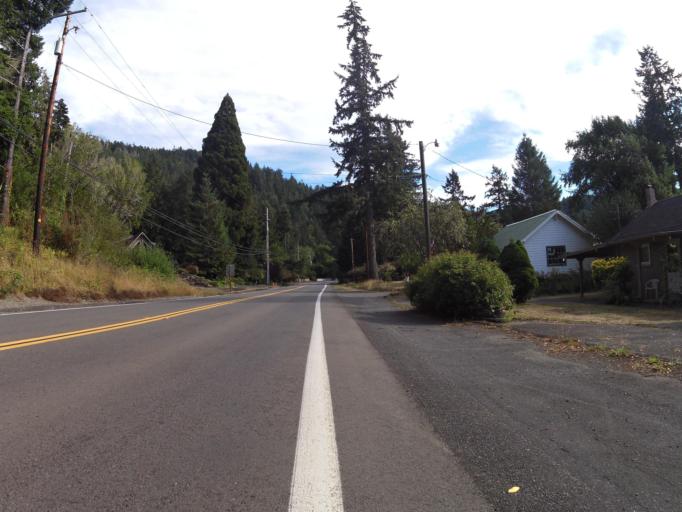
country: US
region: California
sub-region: Del Norte County
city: Bertsch-Oceanview
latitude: 41.8123
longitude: -124.0805
